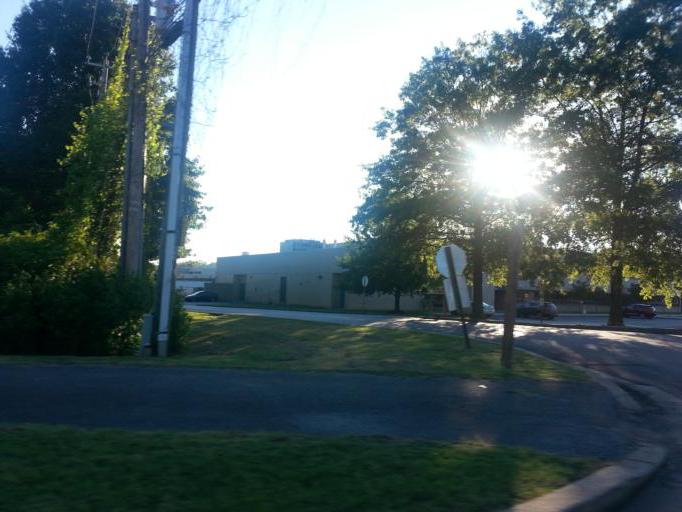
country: US
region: Tennessee
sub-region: Knox County
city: Knoxville
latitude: 35.9489
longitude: -84.0133
